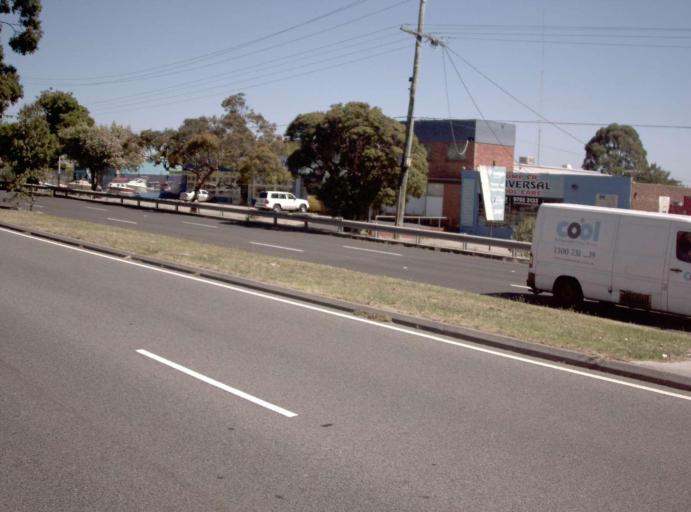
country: AU
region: Victoria
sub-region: Greater Dandenong
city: Dandenong North
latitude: -37.9699
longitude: 145.1979
